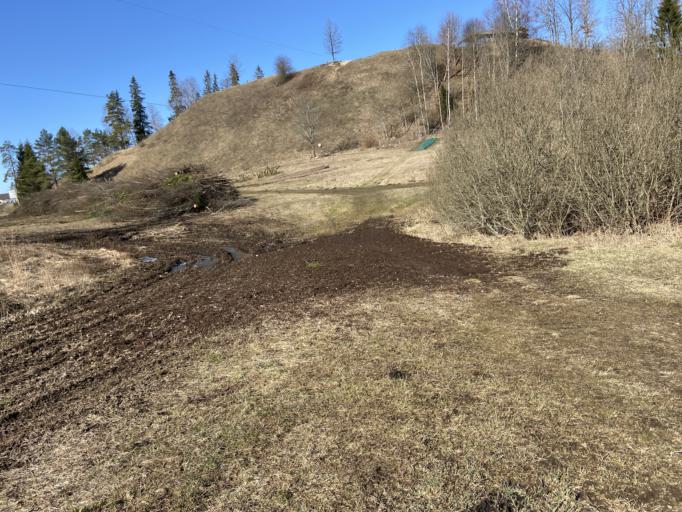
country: EE
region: Tartu
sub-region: Elva linn
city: Elva
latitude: 58.0563
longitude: 26.5063
